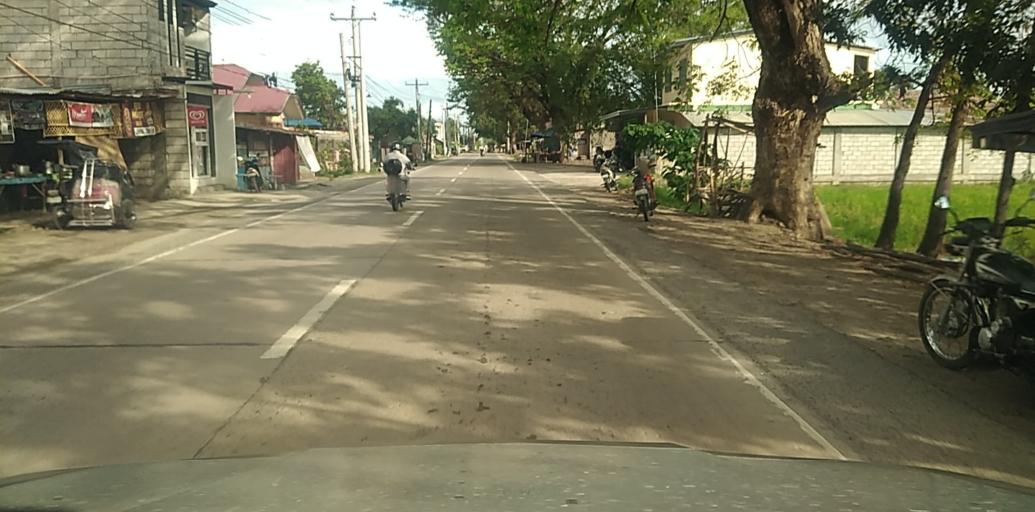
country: PH
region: Central Luzon
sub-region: Province of Pampanga
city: Anao
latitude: 15.1545
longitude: 120.7236
